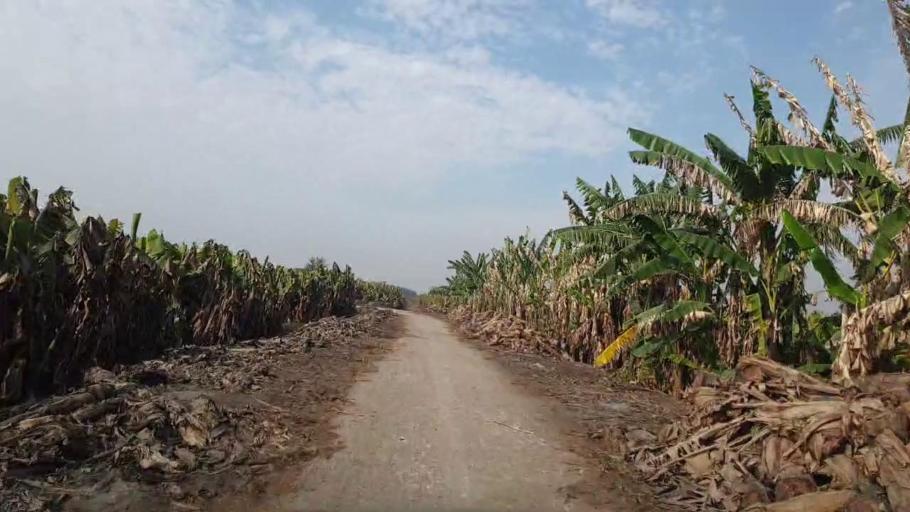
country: PK
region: Sindh
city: Matiari
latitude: 25.5575
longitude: 68.5168
